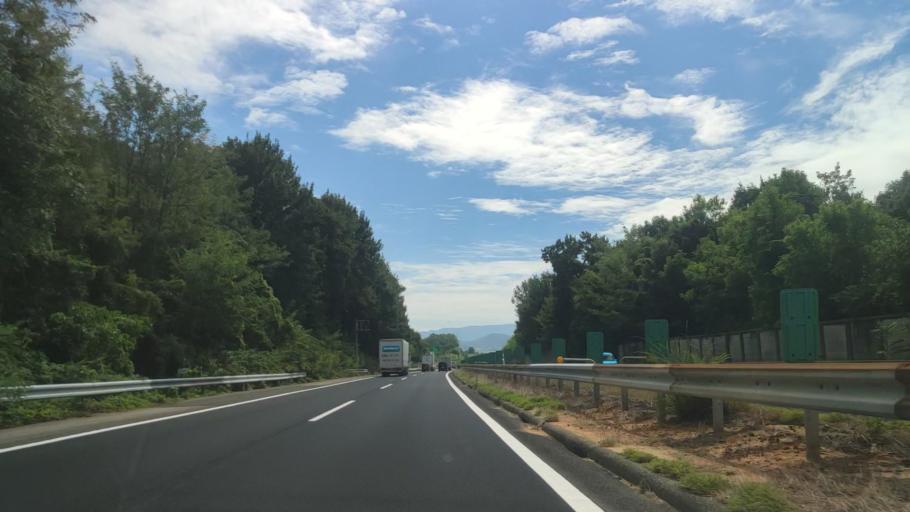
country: JP
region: Aichi
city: Okazaki
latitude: 34.9534
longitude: 137.1960
